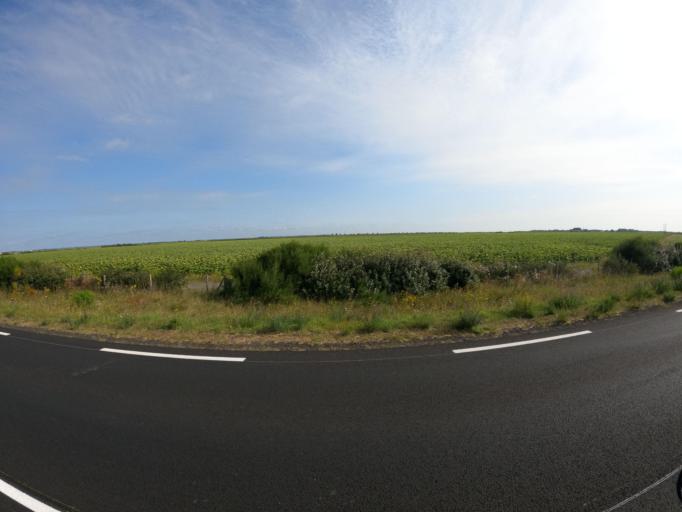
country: FR
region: Pays de la Loire
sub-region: Departement de la Vendee
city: Triaize
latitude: 46.3408
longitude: -1.2924
